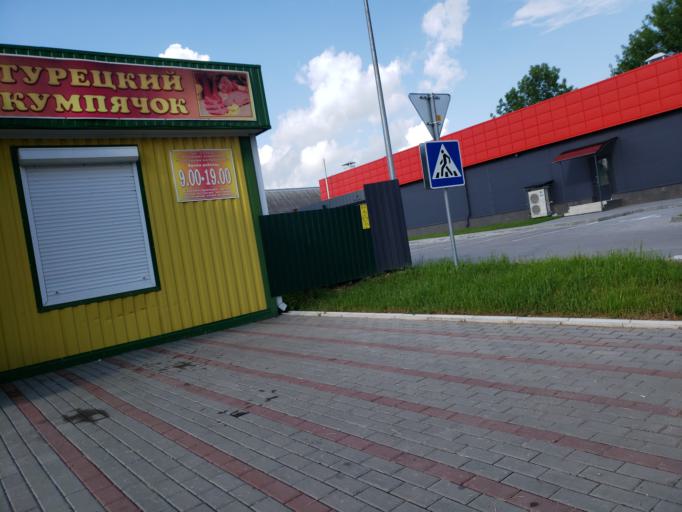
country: BY
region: Minsk
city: Chervyen'
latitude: 53.7085
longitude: 28.4172
